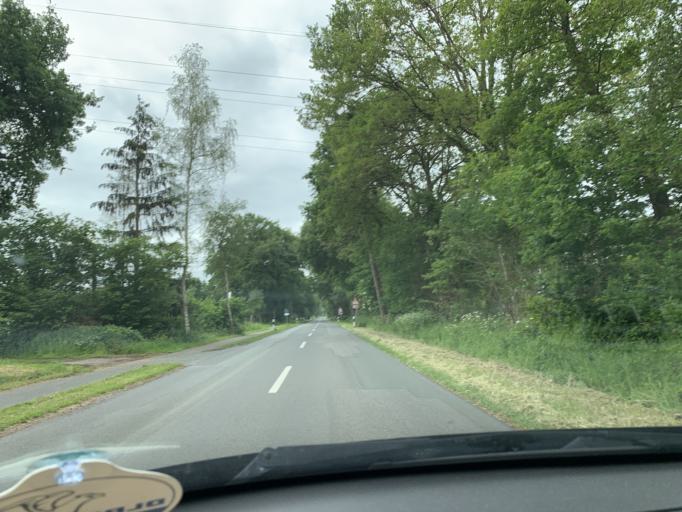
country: DE
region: Lower Saxony
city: Bockhorn
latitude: 53.3434
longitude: 8.0409
